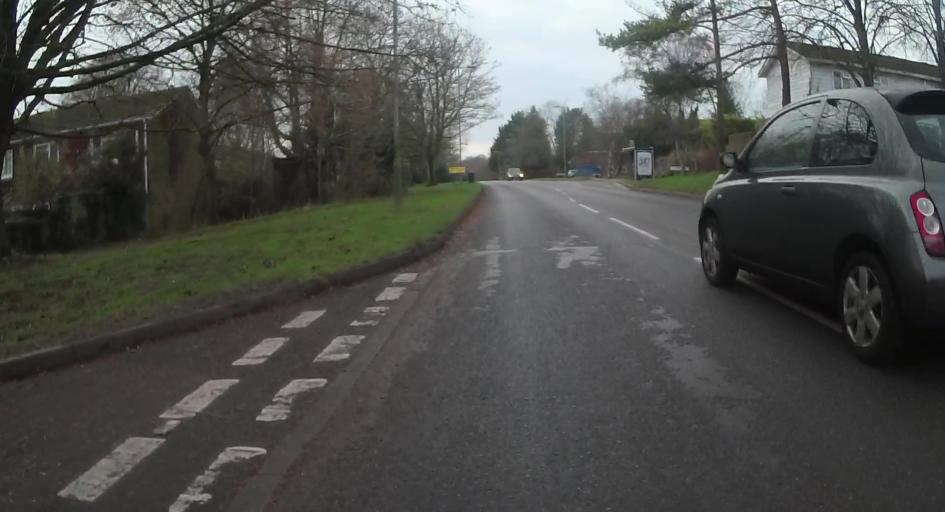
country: GB
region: England
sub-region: Hampshire
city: Basingstoke
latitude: 51.2678
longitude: -1.1219
